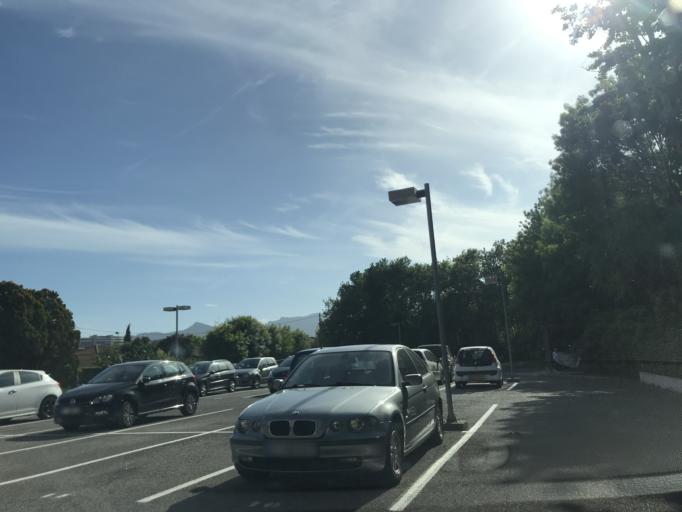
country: FR
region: Provence-Alpes-Cote d'Azur
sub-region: Departement des Alpes-Maritimes
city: Mandelieu-la-Napoule
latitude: 43.5431
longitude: 6.9411
